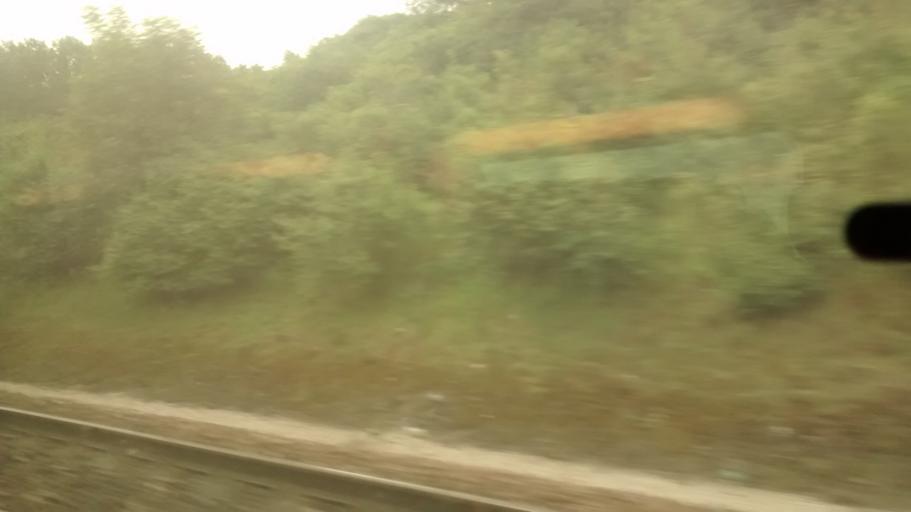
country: FR
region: Ile-de-France
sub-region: Departement de Seine-et-Marne
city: Servon
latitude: 48.7051
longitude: 2.5949
